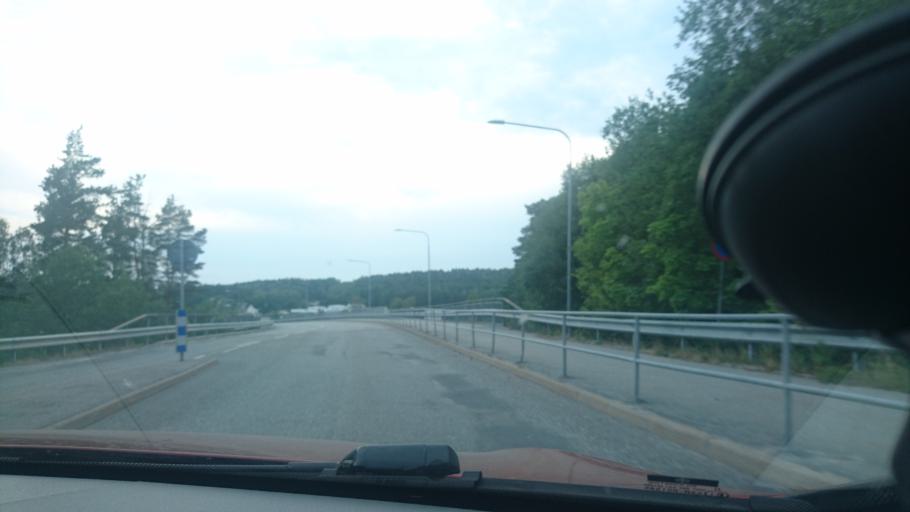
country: SE
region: Stockholm
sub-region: Upplands Vasby Kommun
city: Upplands Vaesby
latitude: 59.5287
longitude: 17.9033
